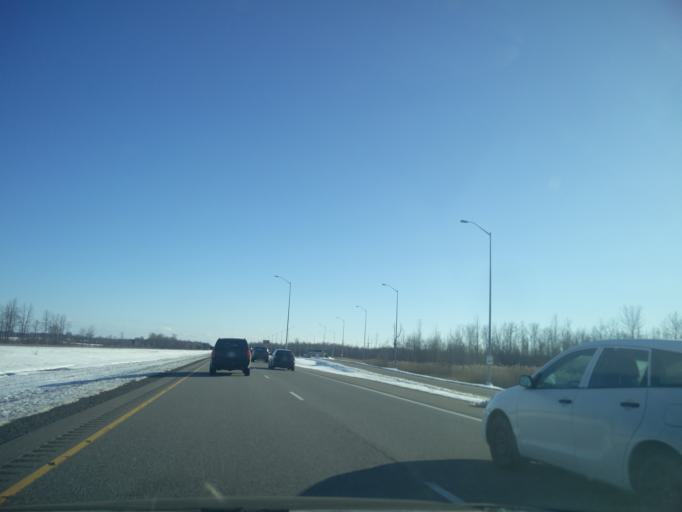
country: CA
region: Ontario
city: Bells Corners
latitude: 45.0588
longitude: -75.6215
